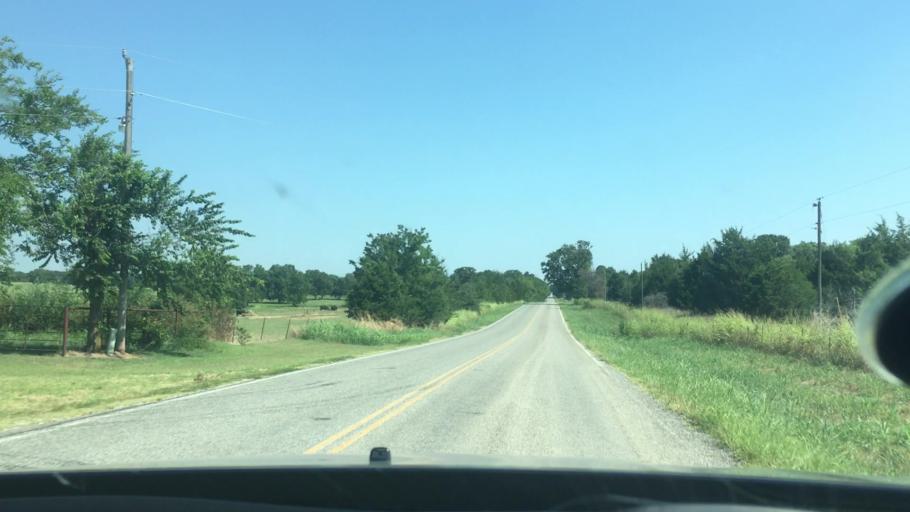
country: US
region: Oklahoma
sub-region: Johnston County
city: Tishomingo
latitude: 34.2790
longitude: -96.6185
